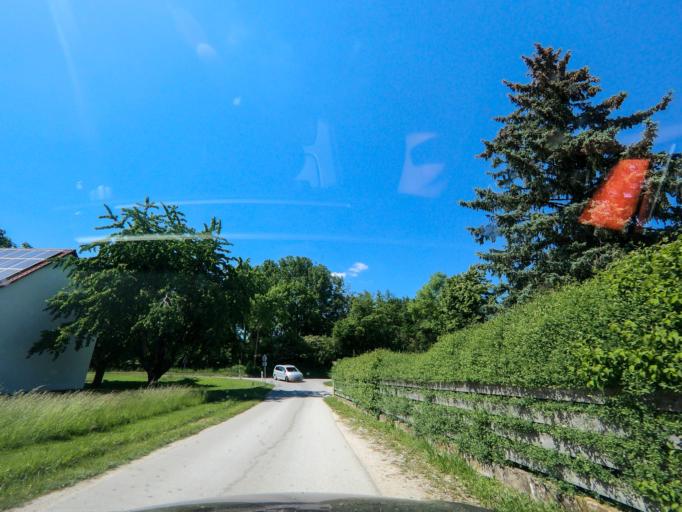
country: DE
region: Bavaria
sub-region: Lower Bavaria
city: Ergolding
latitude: 48.5635
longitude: 12.1785
